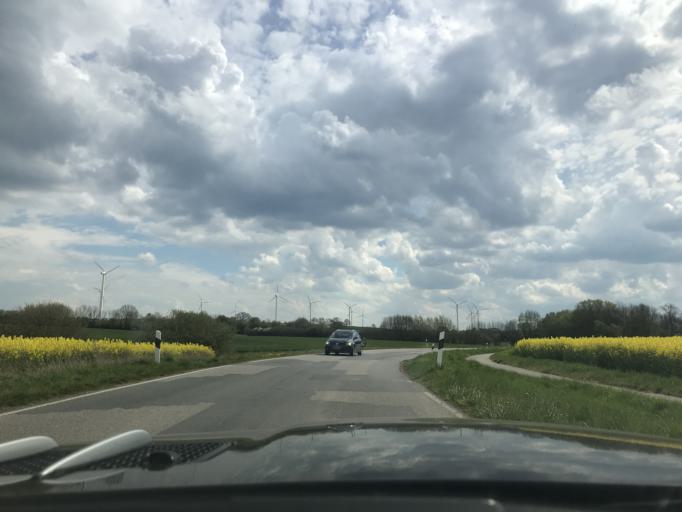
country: DE
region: Schleswig-Holstein
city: Timmendorfer Strand
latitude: 53.9532
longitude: 10.7910
